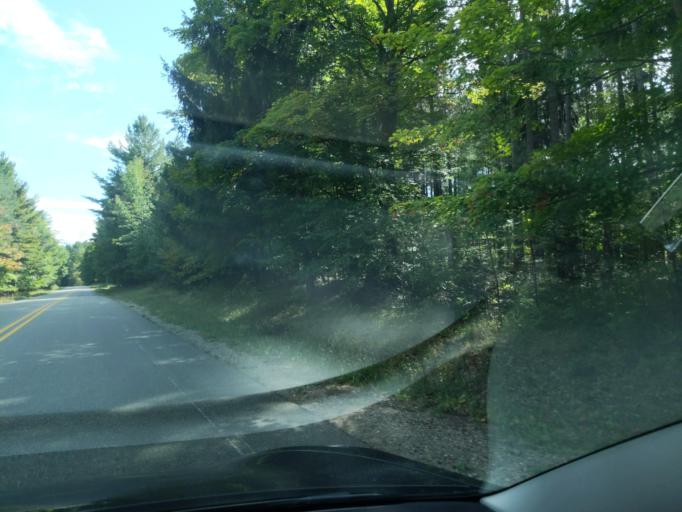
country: US
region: Michigan
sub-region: Antrim County
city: Bellaire
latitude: 45.0535
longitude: -85.3176
